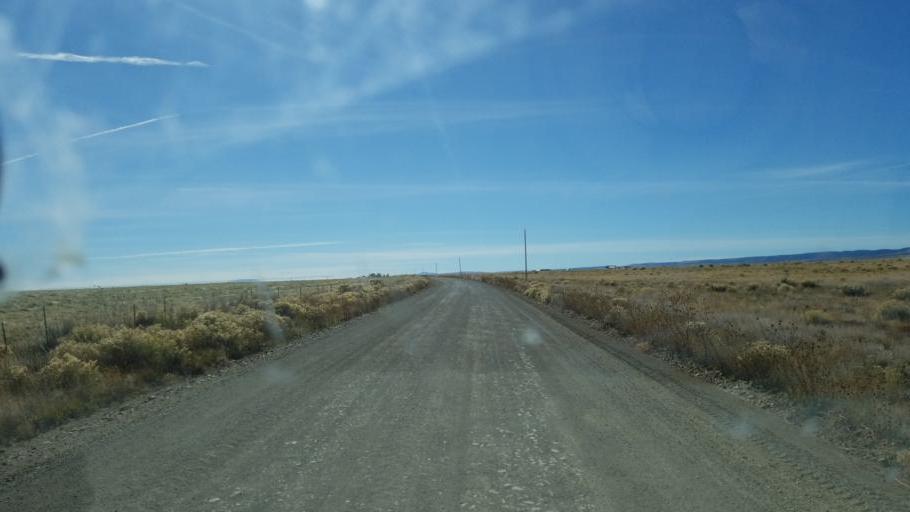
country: US
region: Colorado
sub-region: Rio Grande County
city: Monte Vista
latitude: 37.3980
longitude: -106.1493
